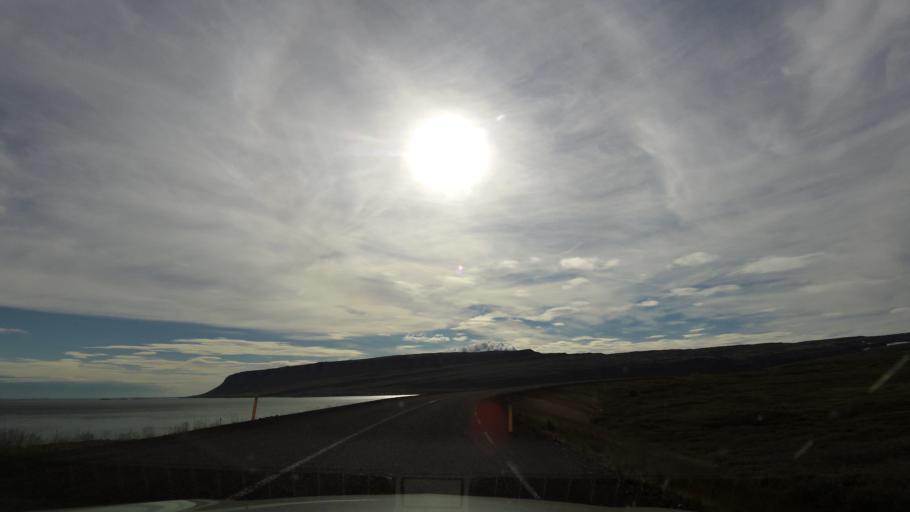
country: IS
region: West
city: Stykkisholmur
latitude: 65.6075
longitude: -22.7737
